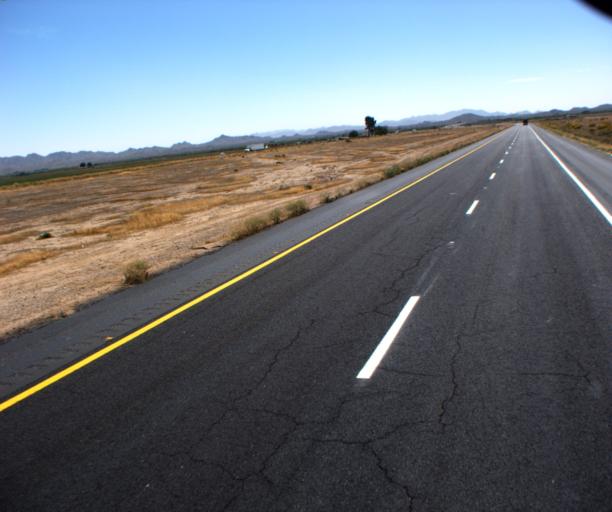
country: US
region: Arizona
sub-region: Maricopa County
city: Buckeye
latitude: 33.3655
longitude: -112.6265
